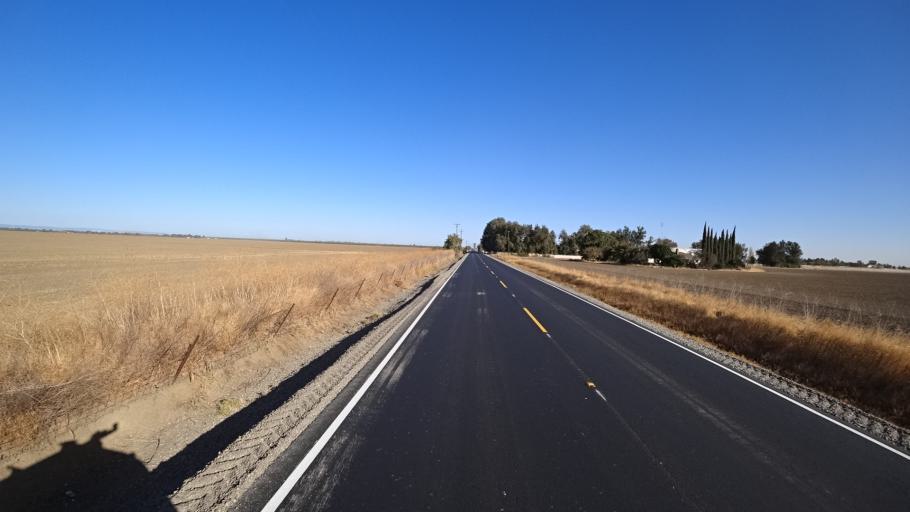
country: US
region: California
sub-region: Yolo County
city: Davis
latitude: 38.5640
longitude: -121.7862
